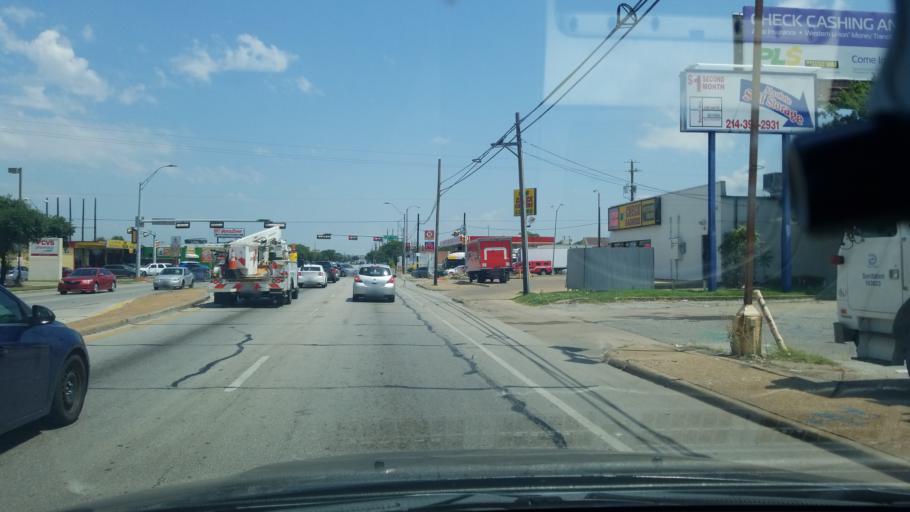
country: US
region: Texas
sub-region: Dallas County
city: Balch Springs
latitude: 32.7334
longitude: -96.6828
